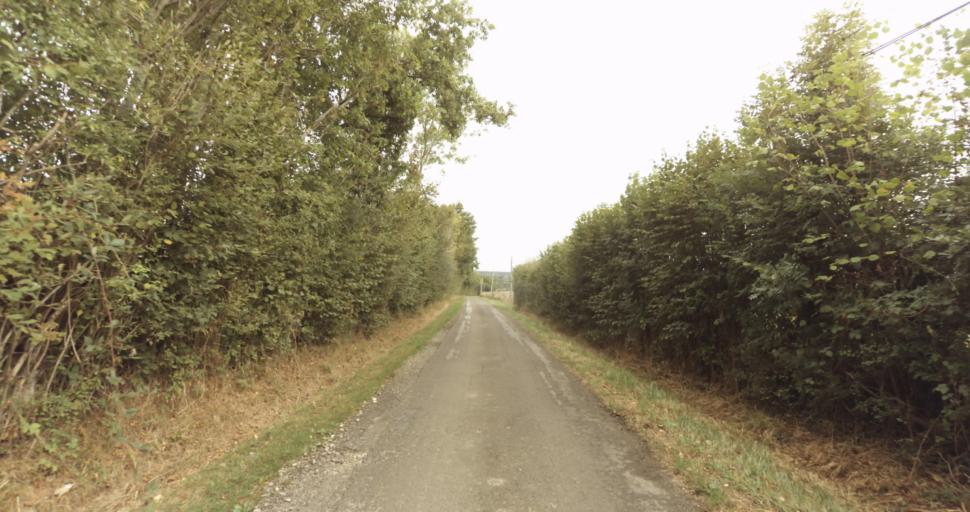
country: FR
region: Lower Normandy
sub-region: Departement de l'Orne
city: Sainte-Gauburge-Sainte-Colombe
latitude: 48.7246
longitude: 0.4786
